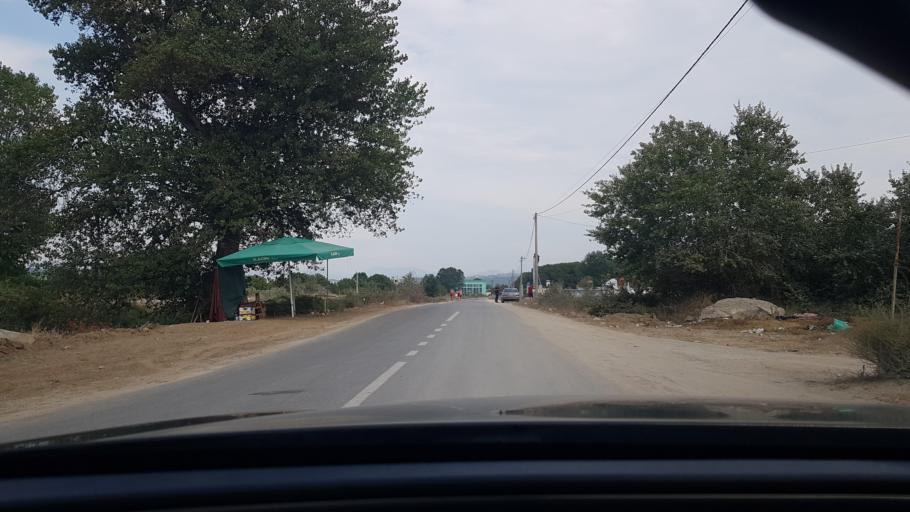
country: AL
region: Durres
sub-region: Rrethi i Durresit
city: Katundi i Ri
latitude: 41.4871
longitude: 19.5130
